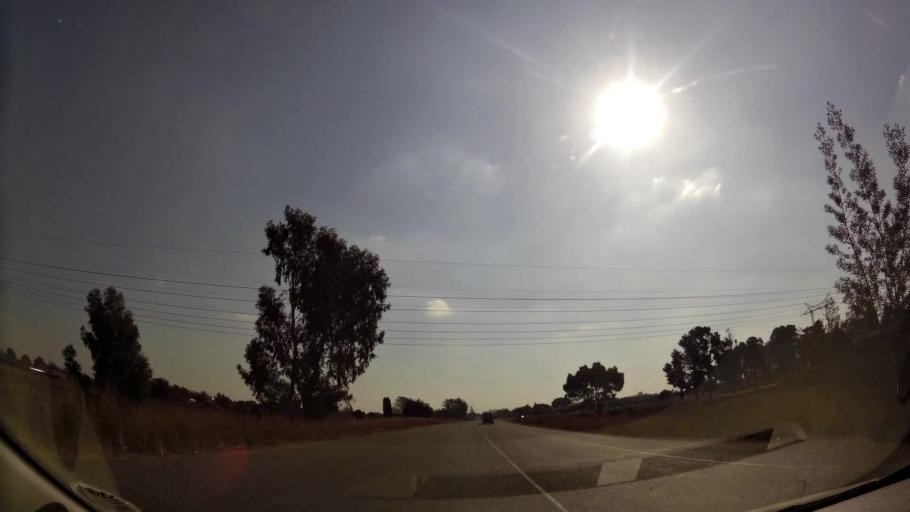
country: ZA
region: Gauteng
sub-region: West Rand District Municipality
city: Randfontein
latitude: -26.1761
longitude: 27.7102
